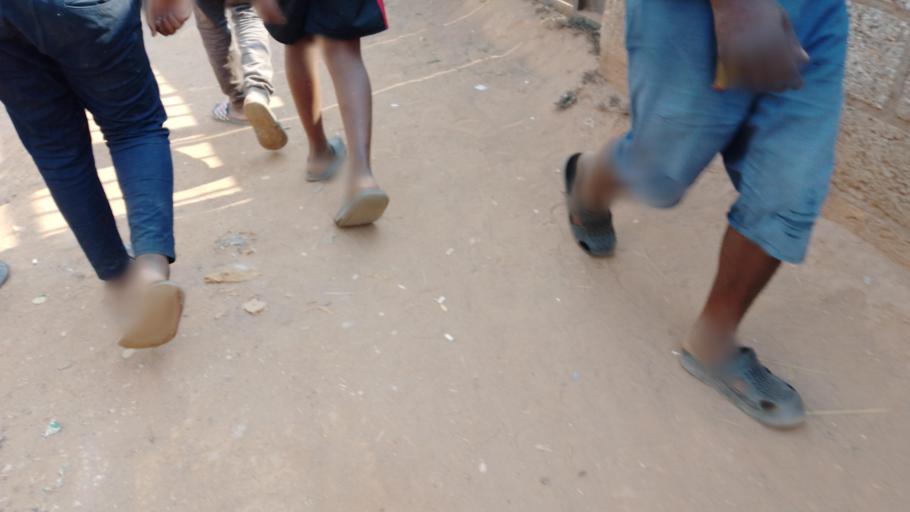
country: ZM
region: Lusaka
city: Lusaka
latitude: -15.3967
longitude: 28.3729
